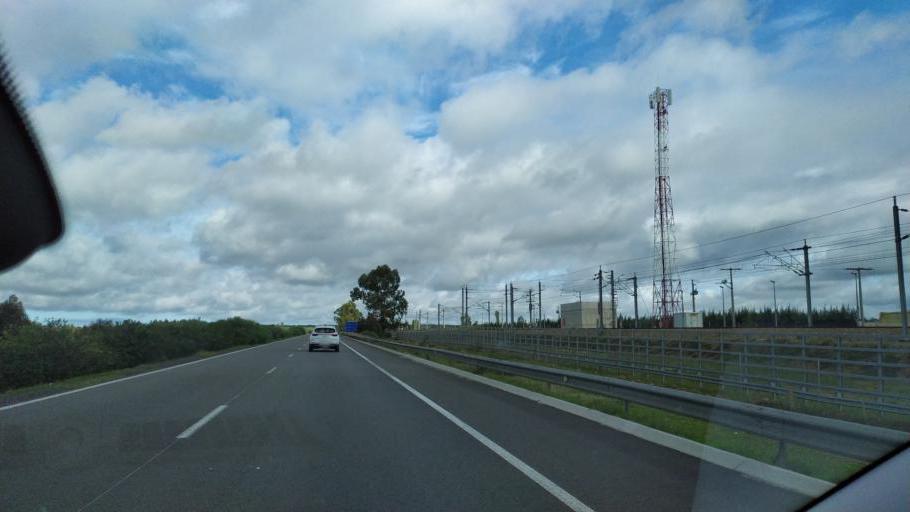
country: MA
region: Gharb-Chrarda-Beni Hssen
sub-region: Kenitra Province
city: Lalla Mimouna
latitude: 34.8882
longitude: -6.2101
